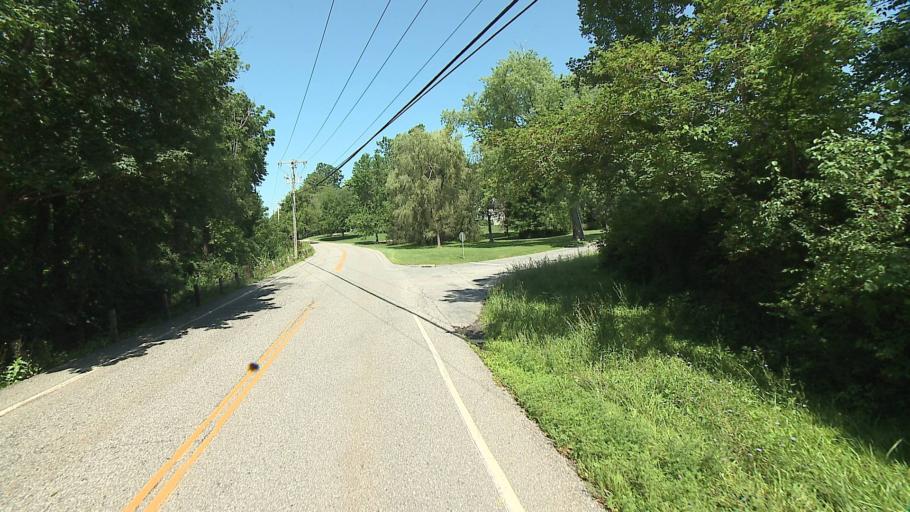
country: US
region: Connecticut
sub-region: Litchfield County
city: Kent
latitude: 41.8918
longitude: -73.4816
